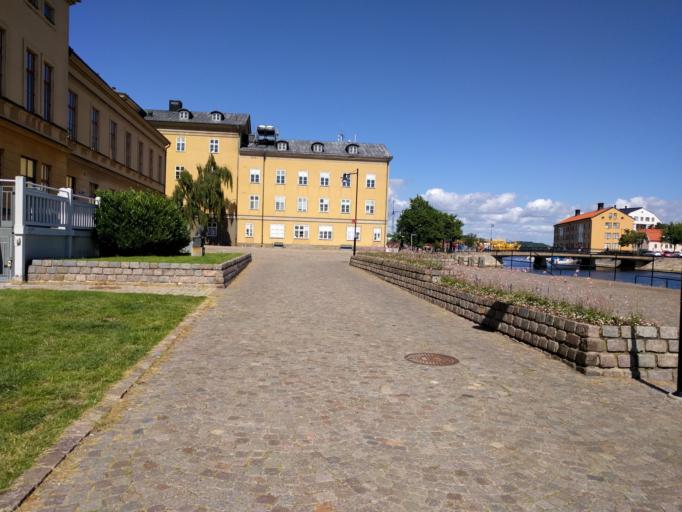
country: SE
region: Blekinge
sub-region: Karlskrona Kommun
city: Karlskrona
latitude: 56.1601
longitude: 15.5950
